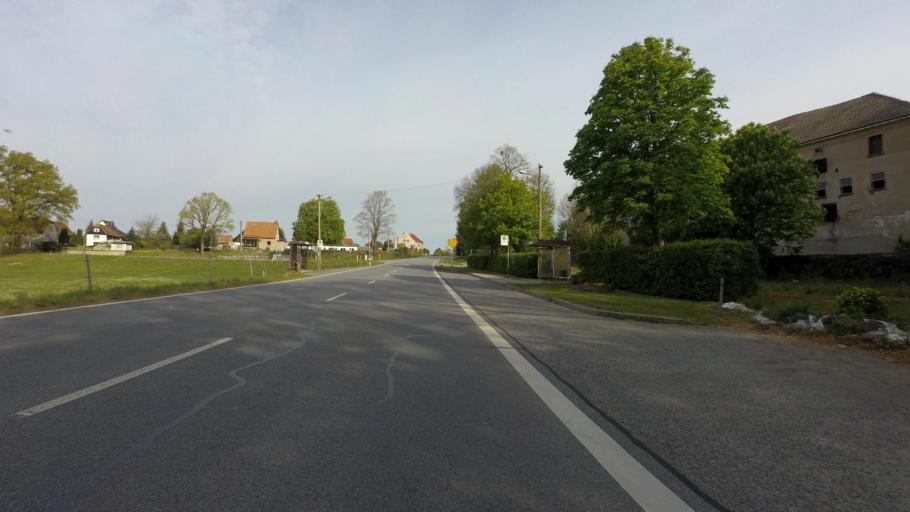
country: DE
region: Saxony
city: Stolpen
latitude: 51.0568
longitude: 14.0636
